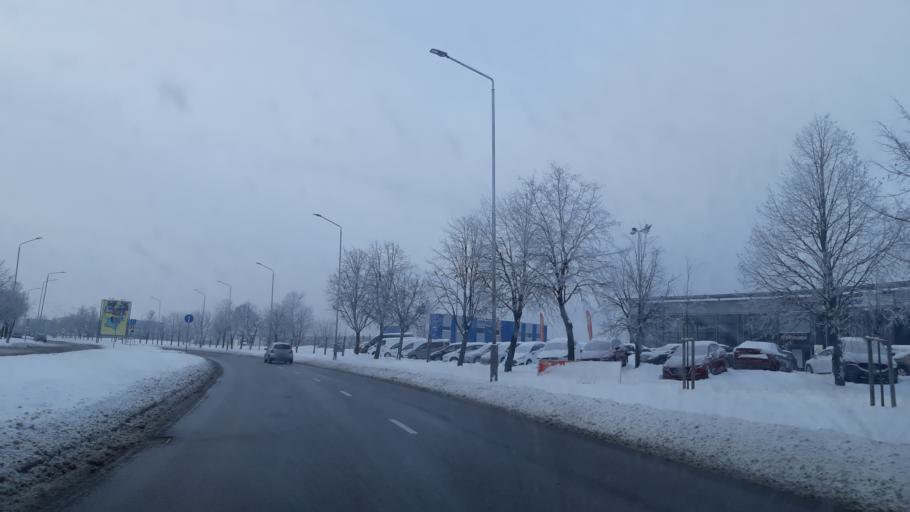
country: LT
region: Kauno apskritis
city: Dainava (Kaunas)
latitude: 54.9304
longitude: 23.9687
